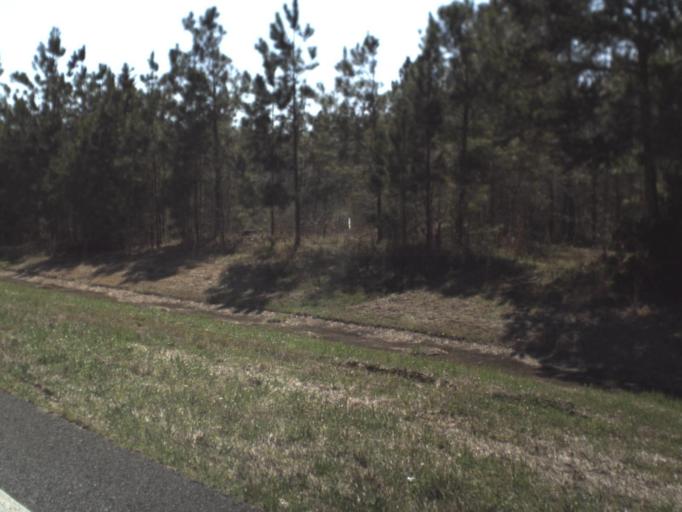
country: US
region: Florida
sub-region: Jackson County
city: Graceville
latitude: 30.8828
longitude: -85.3657
